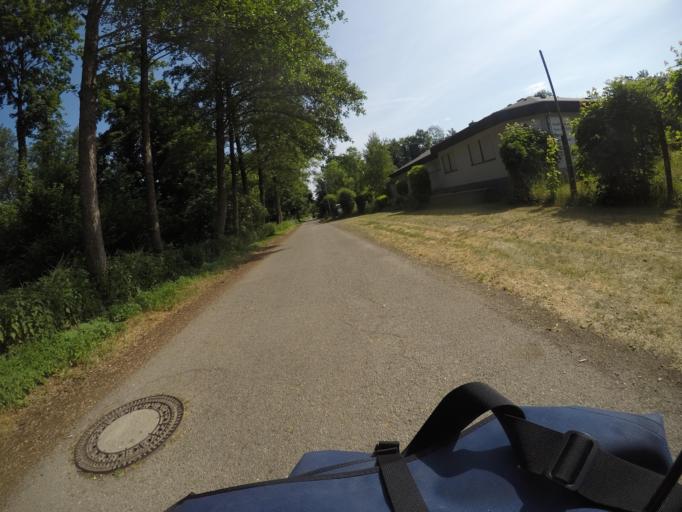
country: DE
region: Baden-Wuerttemberg
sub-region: Karlsruhe Region
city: Bietigheim
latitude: 48.9202
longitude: 8.2485
